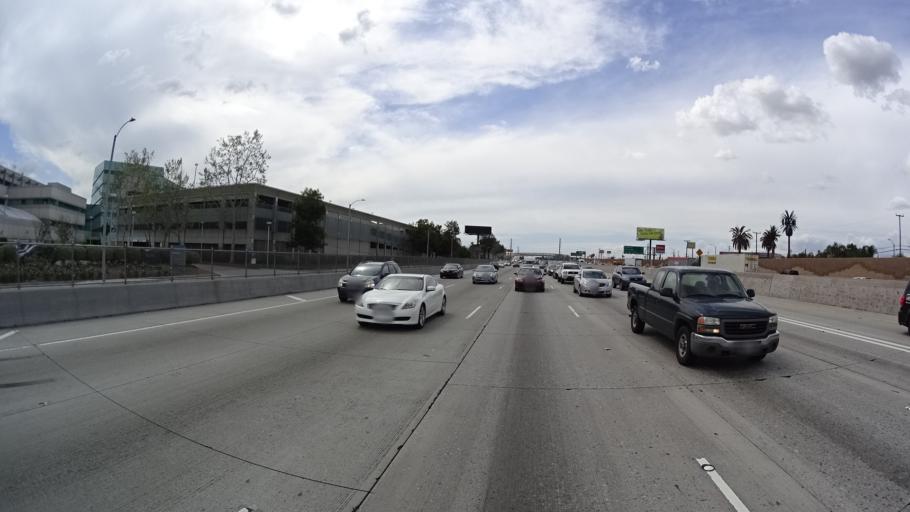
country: US
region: California
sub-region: Los Angeles County
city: West Puente Valley
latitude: 34.0670
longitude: -117.9850
